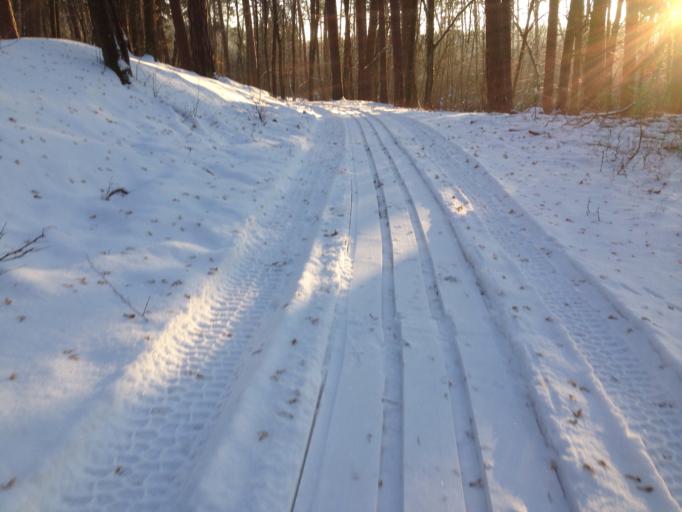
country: PL
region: Kujawsko-Pomorskie
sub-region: Powiat brodnicki
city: Gorzno
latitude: 53.1837
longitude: 19.6777
